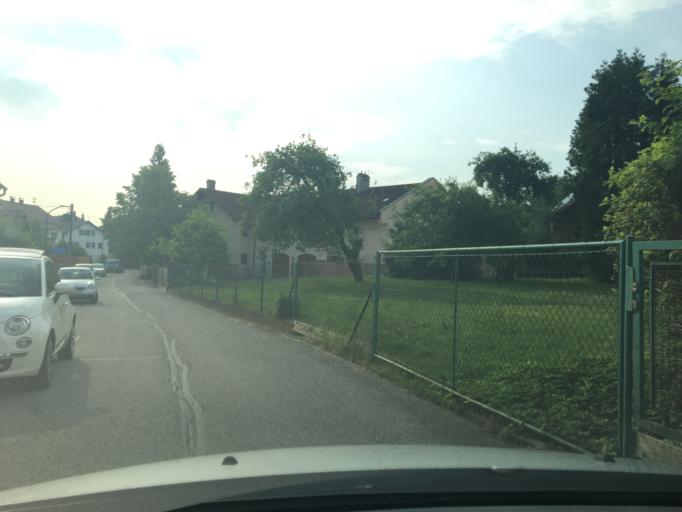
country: DE
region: Bavaria
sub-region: Upper Bavaria
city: Neumarkt-Sankt Veit
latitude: 48.3614
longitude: 12.5098
